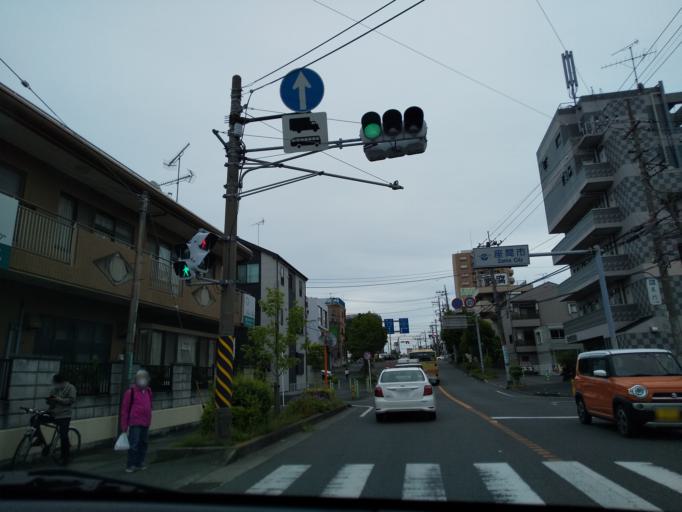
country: JP
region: Kanagawa
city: Zama
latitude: 35.5091
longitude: 139.4132
